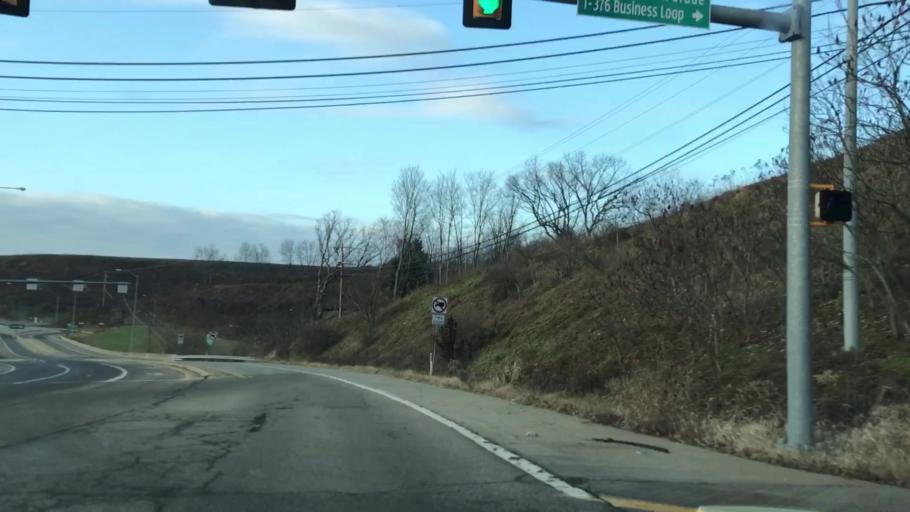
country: US
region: Pennsylvania
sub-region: Allegheny County
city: Carnot-Moon
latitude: 40.4829
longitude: -80.2000
